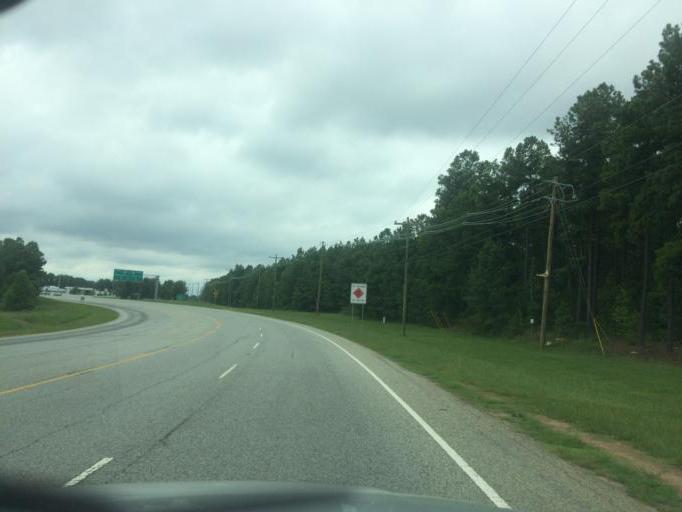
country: US
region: South Carolina
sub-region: Greenville County
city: Greer
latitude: 34.8940
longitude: -82.1974
